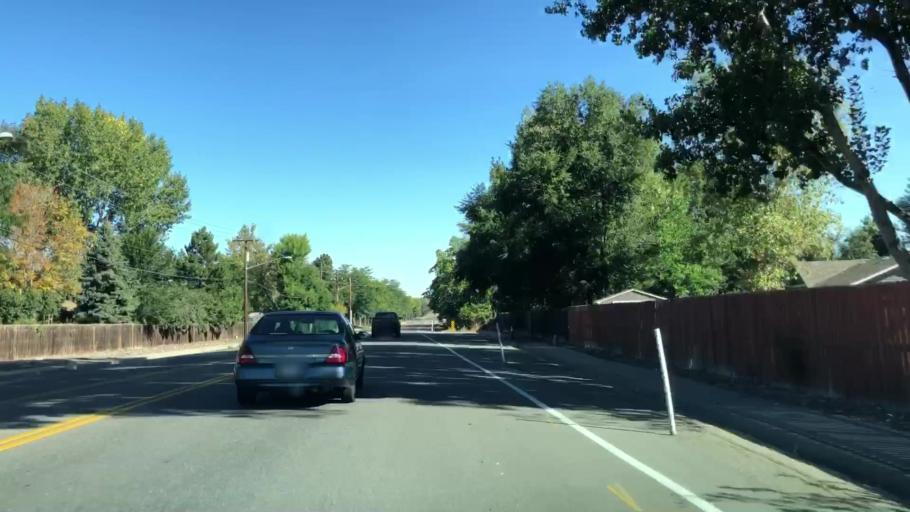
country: US
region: Colorado
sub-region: Larimer County
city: Loveland
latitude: 40.4171
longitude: -105.0586
